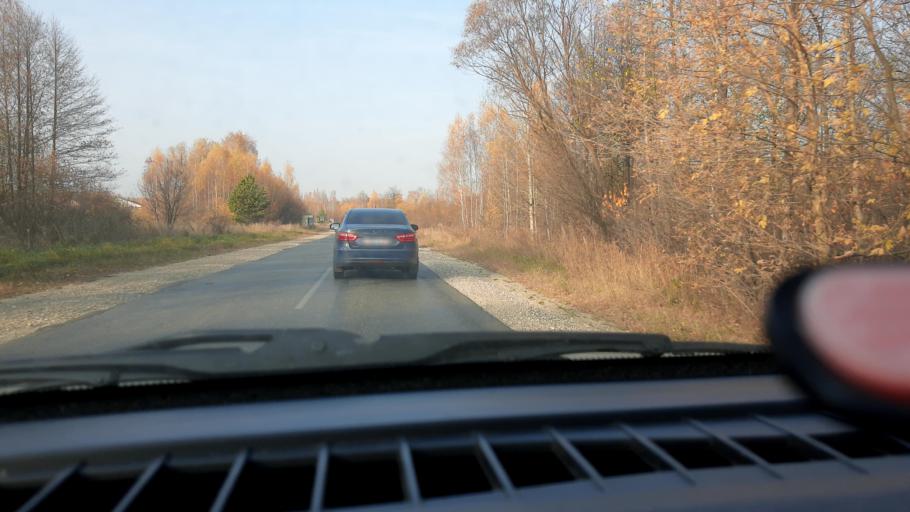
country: RU
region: Nizjnij Novgorod
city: Neklyudovo
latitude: 56.4337
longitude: 43.9221
